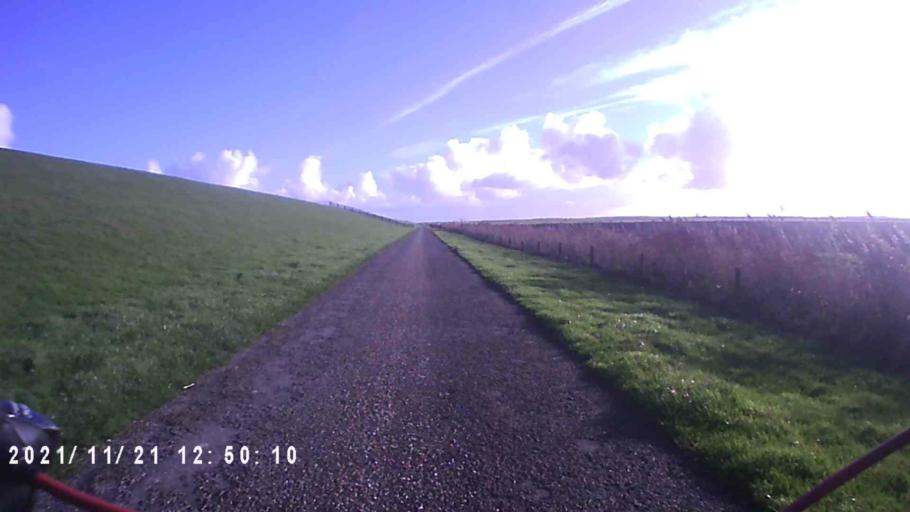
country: NL
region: Friesland
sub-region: Gemeente Dongeradeel
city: Anjum
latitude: 53.4008
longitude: 6.1181
